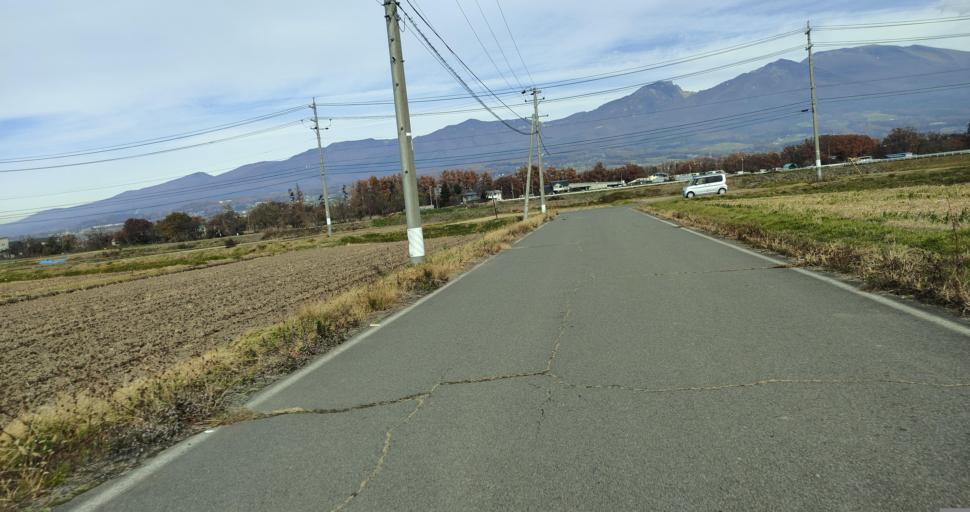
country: JP
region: Nagano
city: Komoro
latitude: 36.3044
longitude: 138.4726
